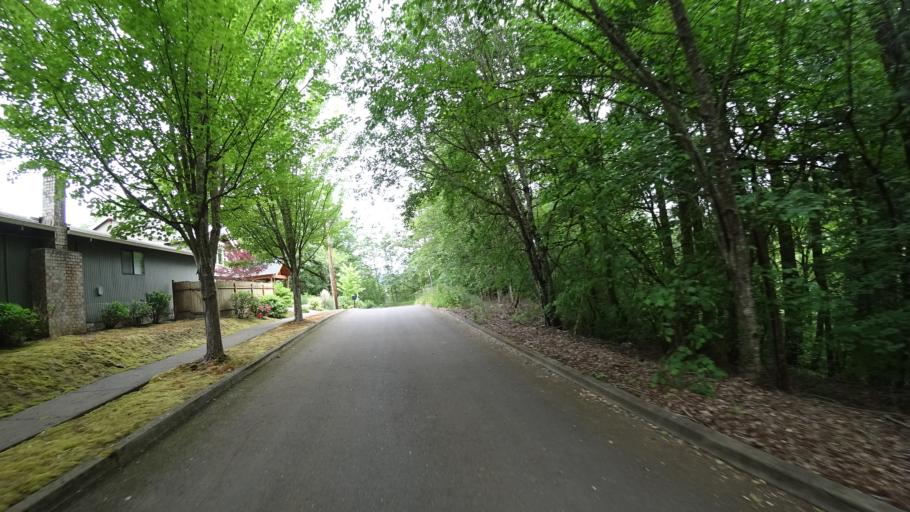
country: US
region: Oregon
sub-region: Washington County
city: Garden Home-Whitford
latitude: 45.4604
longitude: -122.7263
